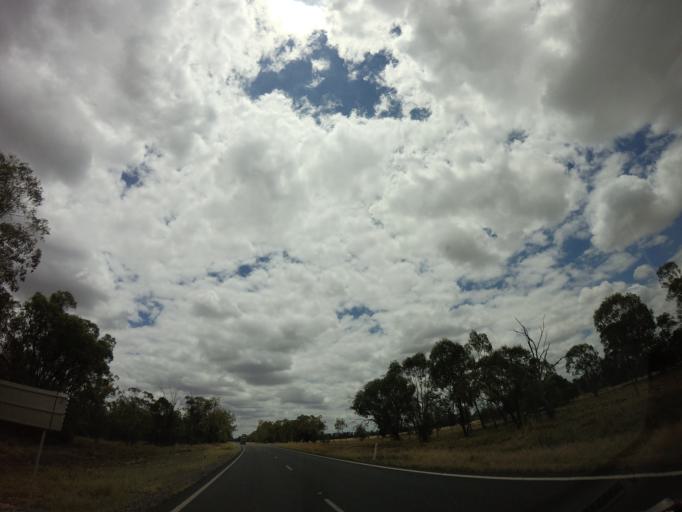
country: AU
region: Queensland
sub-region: Goondiwindi
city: Goondiwindi
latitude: -28.4594
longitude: 150.2963
